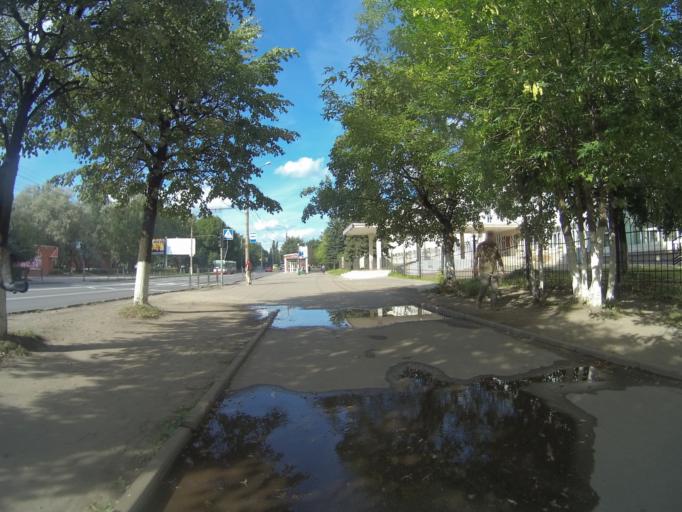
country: RU
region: Vladimir
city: Vladimir
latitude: 56.1374
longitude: 40.3631
